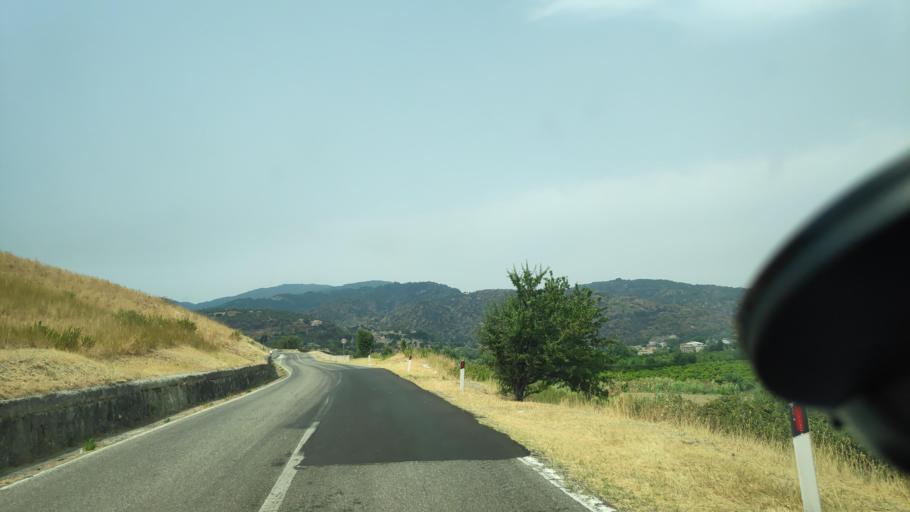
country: IT
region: Calabria
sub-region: Provincia di Catanzaro
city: Marina di Davoli
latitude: 38.6510
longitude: 16.5431
